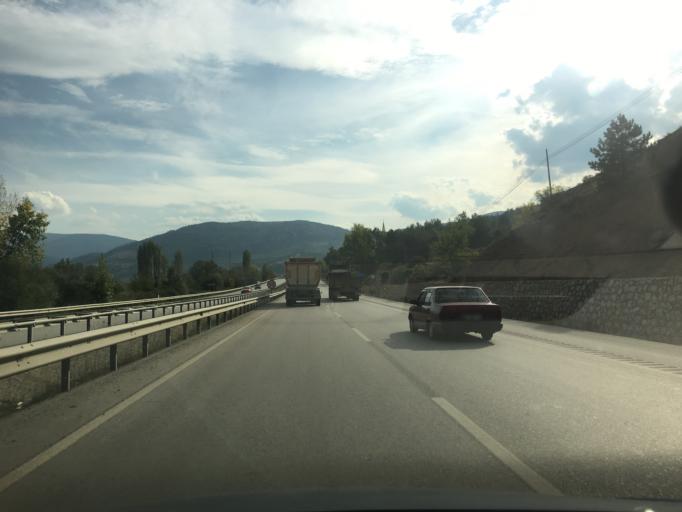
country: TR
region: Karabuk
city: Karabuk
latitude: 41.1156
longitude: 32.6718
